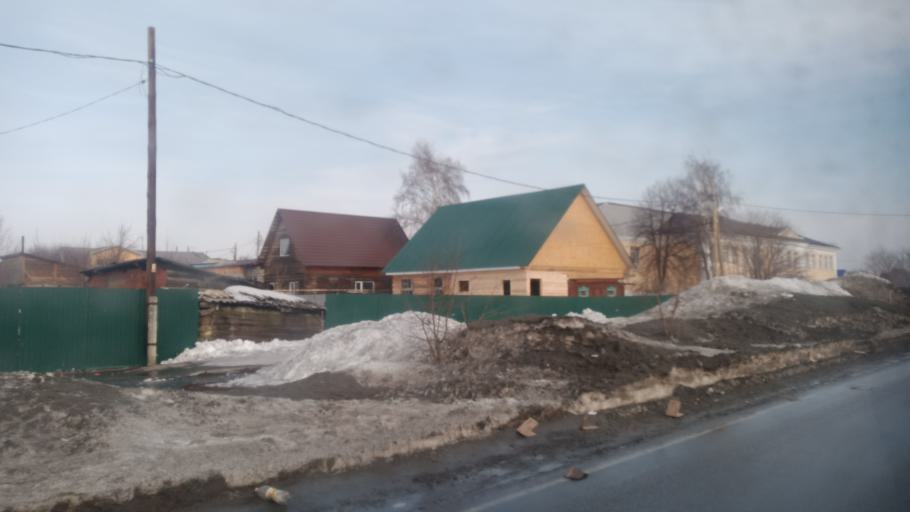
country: RU
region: Altai Krai
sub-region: Gorod Barnaulskiy
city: Barnaul
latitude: 53.3494
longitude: 83.7428
